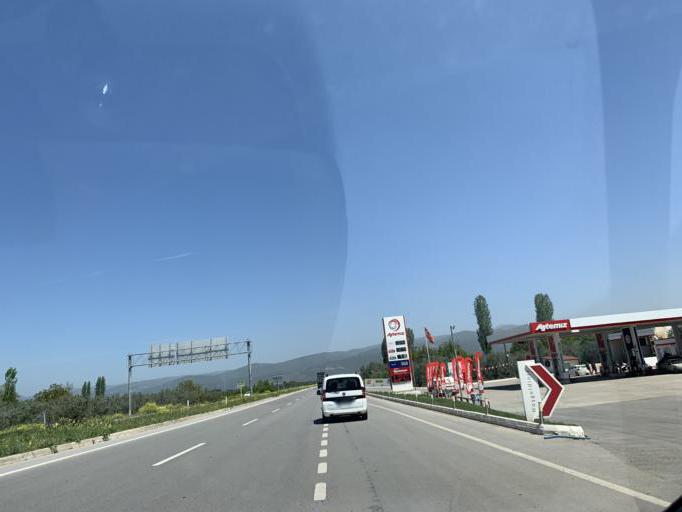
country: TR
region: Bursa
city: Iznik
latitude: 40.3983
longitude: 29.6946
